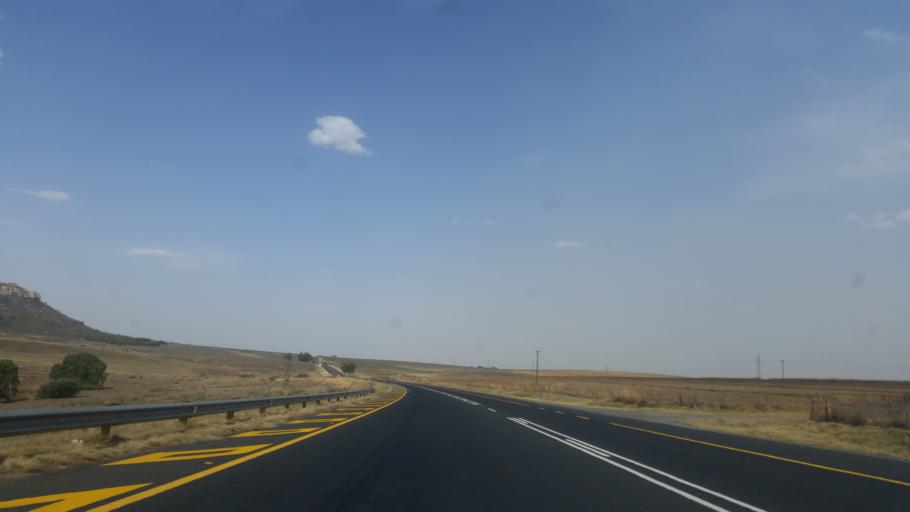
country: ZA
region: Orange Free State
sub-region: Thabo Mofutsanyana District Municipality
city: Bethlehem
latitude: -28.3004
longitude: 28.5473
